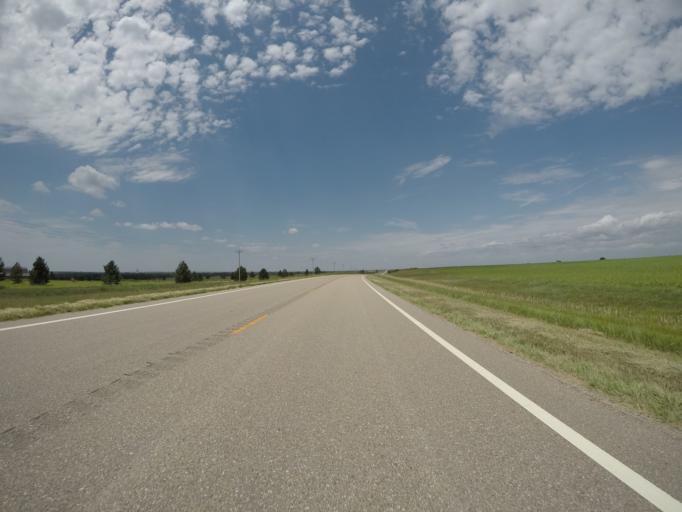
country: US
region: Kansas
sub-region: Graham County
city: Hill City
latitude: 39.3800
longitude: -99.6691
